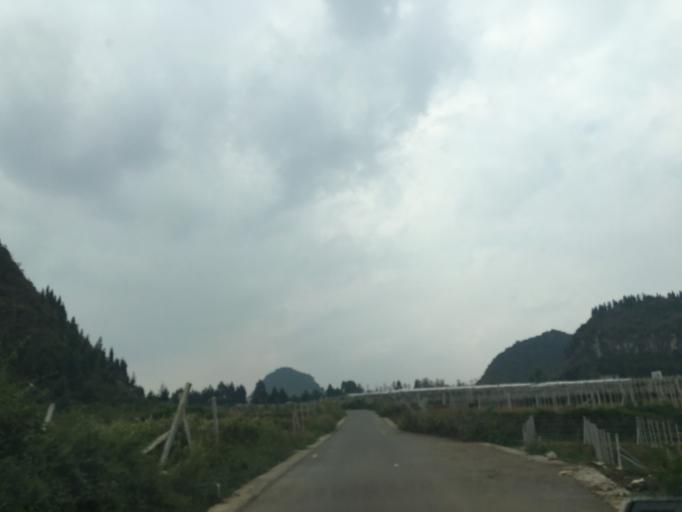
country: CN
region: Guangxi Zhuangzu Zizhiqu
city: Xinzhou
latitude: 25.4833
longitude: 105.6474
